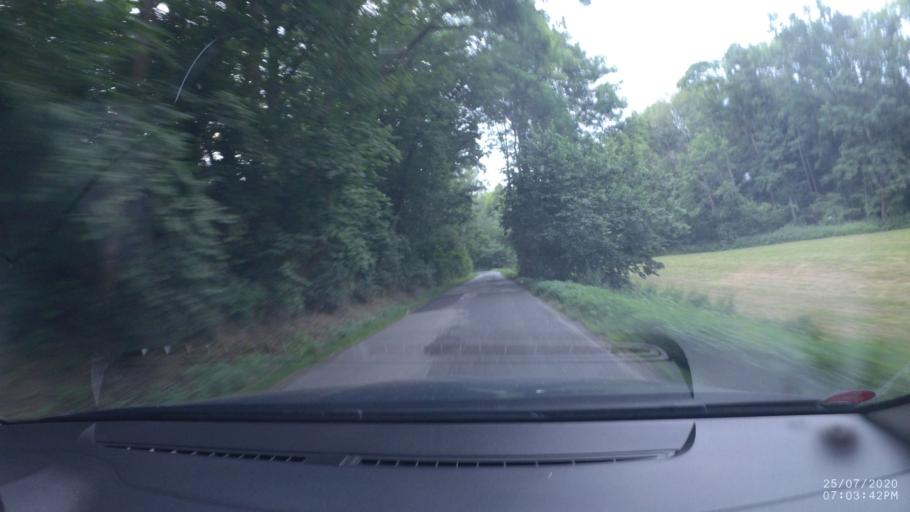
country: CZ
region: Kralovehradecky
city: Horice
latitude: 50.3600
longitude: 15.6637
